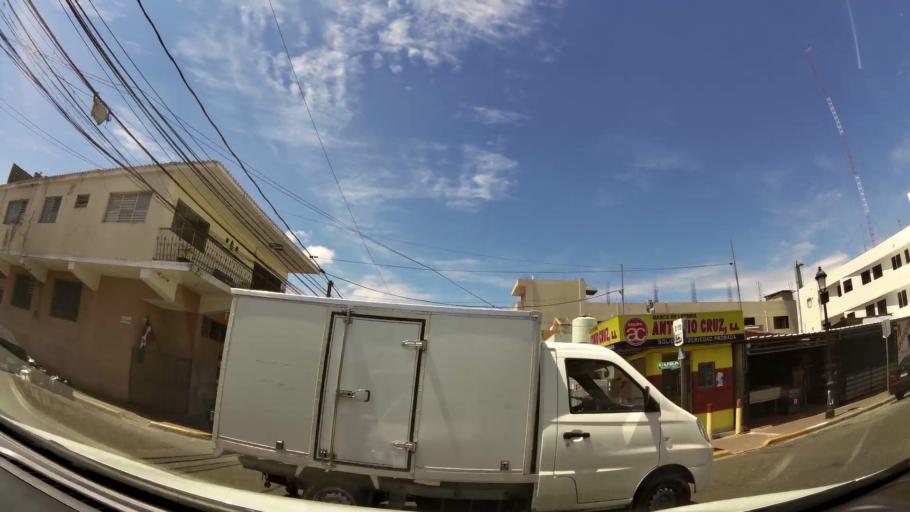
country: DO
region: Santiago
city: Santiago de los Caballeros
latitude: 19.4492
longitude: -70.7003
